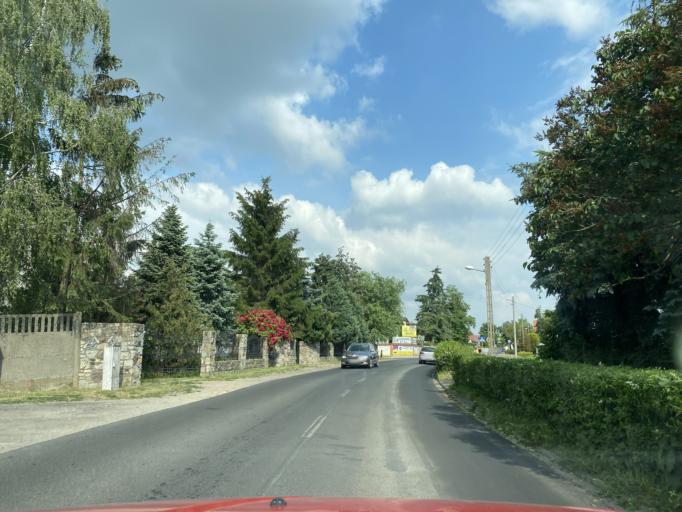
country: PL
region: Greater Poland Voivodeship
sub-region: Powiat poznanski
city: Dopiewo
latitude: 52.3602
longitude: 16.7067
